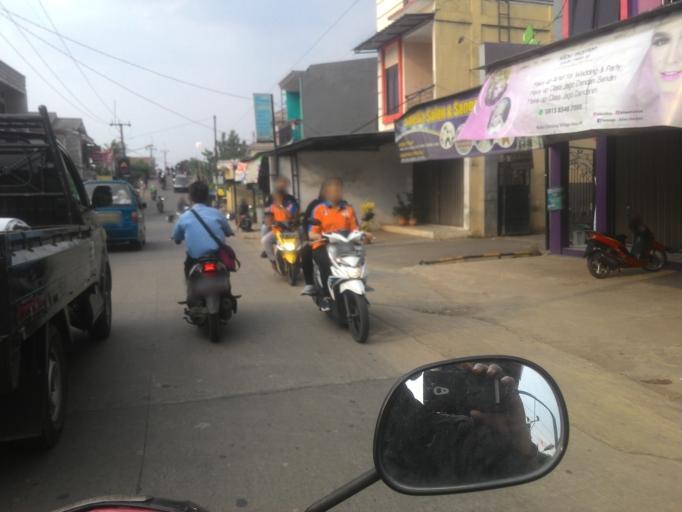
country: ID
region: West Java
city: Cibinong
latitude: -6.4644
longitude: 106.8396
